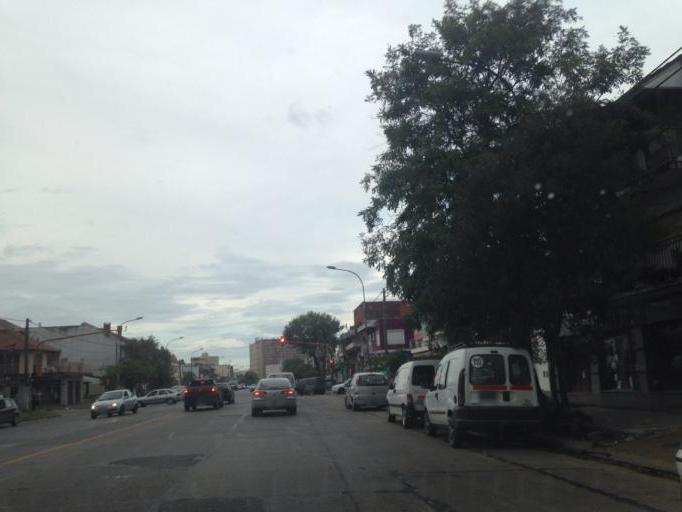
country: AR
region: Buenos Aires
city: Mar del Plata
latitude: -38.0221
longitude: -57.5750
